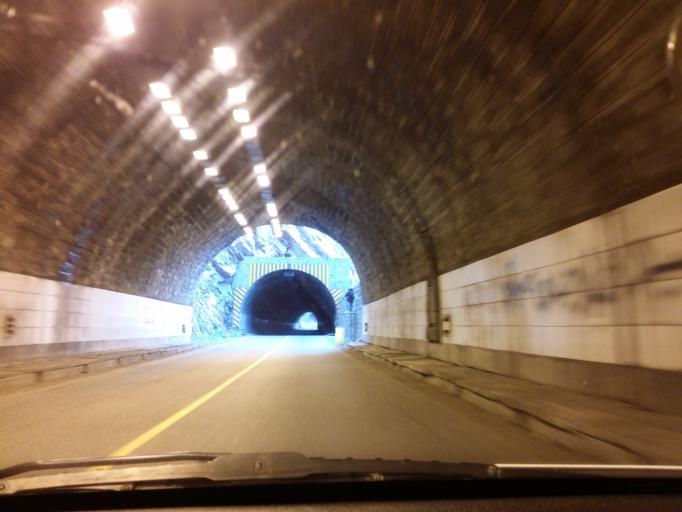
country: IR
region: Mazandaran
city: Chalus
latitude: 36.2624
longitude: 51.2721
